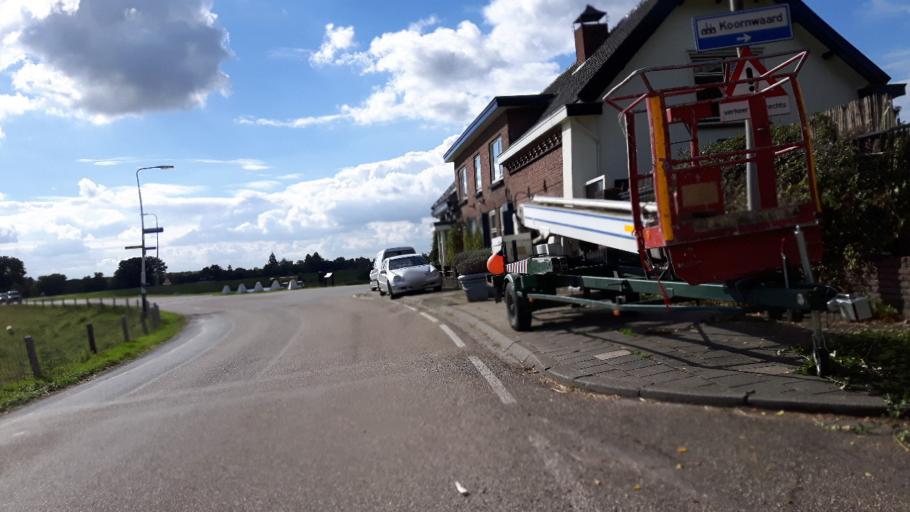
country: NL
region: South Holland
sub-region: Gemeente Leerdam
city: Leerdam
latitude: 51.8609
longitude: 5.0649
